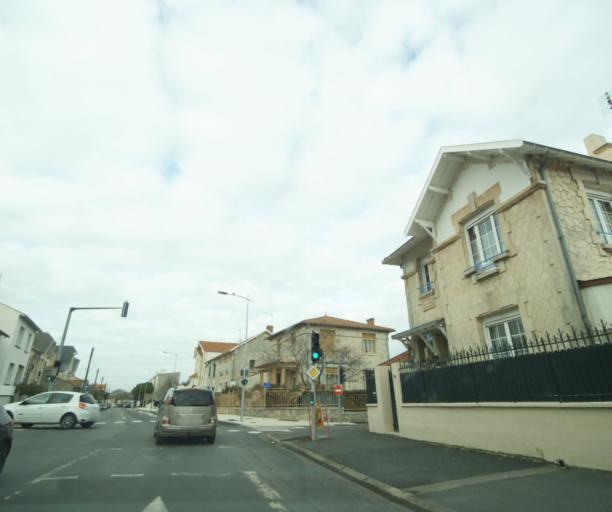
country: FR
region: Poitou-Charentes
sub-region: Departement de la Charente-Maritime
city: La Rochelle
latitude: 46.1672
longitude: -1.1639
